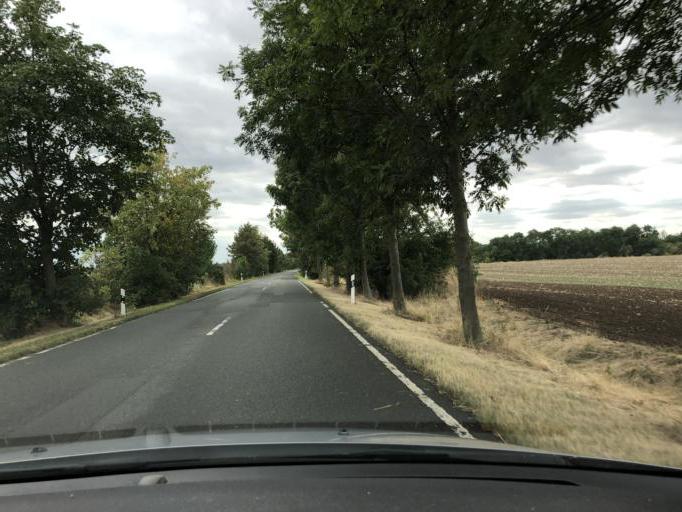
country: DE
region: Saxony-Anhalt
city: Brumby
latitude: 51.8654
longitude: 11.7117
